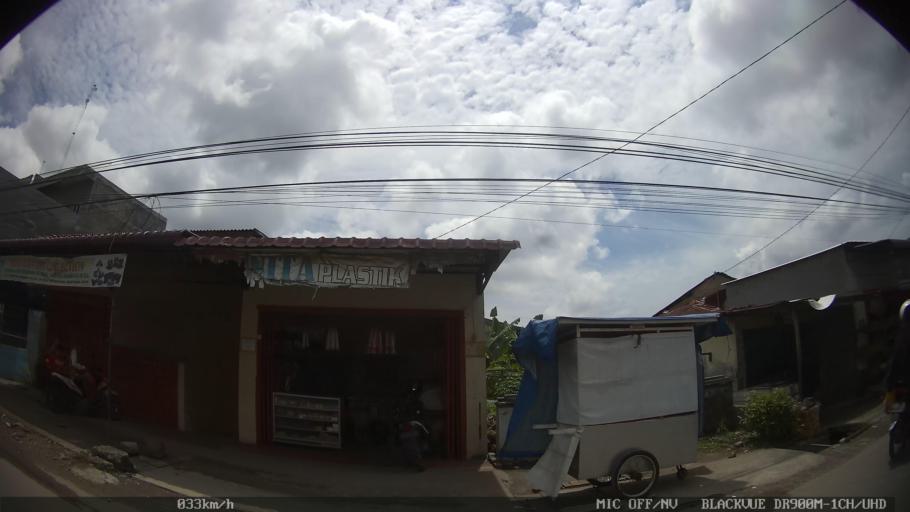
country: ID
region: North Sumatra
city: Medan
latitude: 3.6146
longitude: 98.7481
